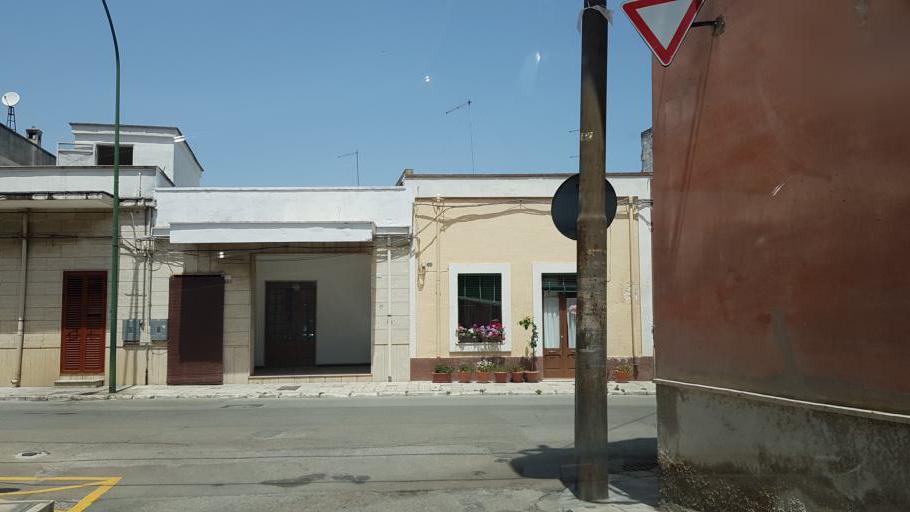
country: IT
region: Apulia
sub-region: Provincia di Brindisi
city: San Pancrazio Salentino
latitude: 40.4170
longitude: 17.8424
